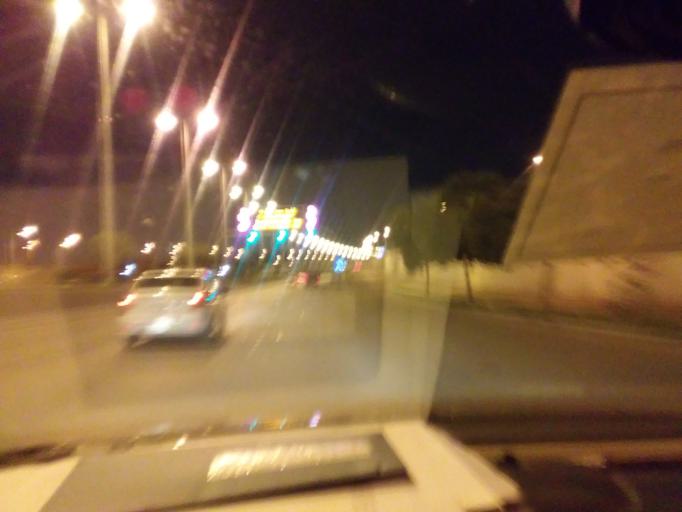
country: SA
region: Ar Riyad
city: Riyadh
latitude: 24.7361
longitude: 46.7424
